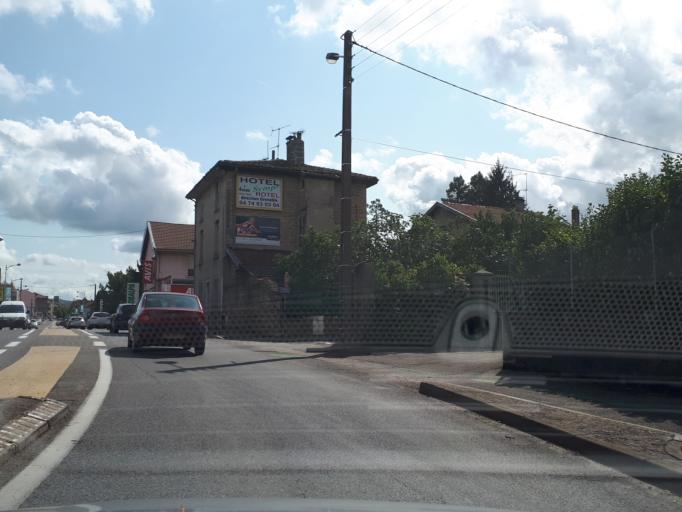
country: FR
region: Rhone-Alpes
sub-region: Departement de l'Isere
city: Bourgoin-Jallieu
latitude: 45.5854
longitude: 5.2610
